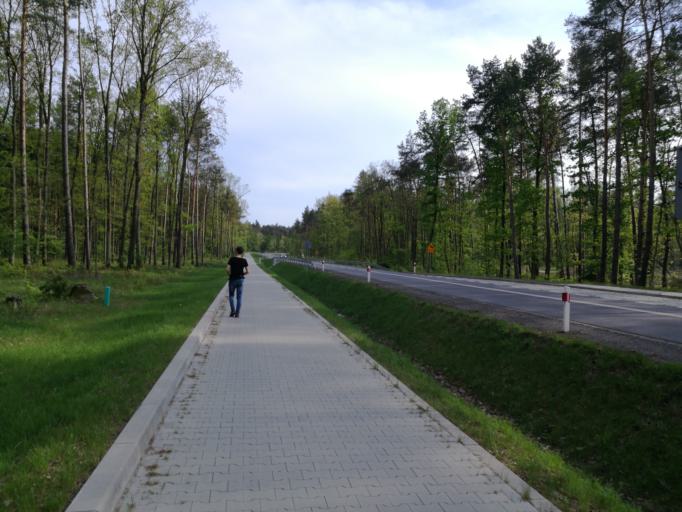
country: PL
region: Lodz Voivodeship
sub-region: Skierniewice
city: Skierniewice
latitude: 52.0008
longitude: 20.1845
